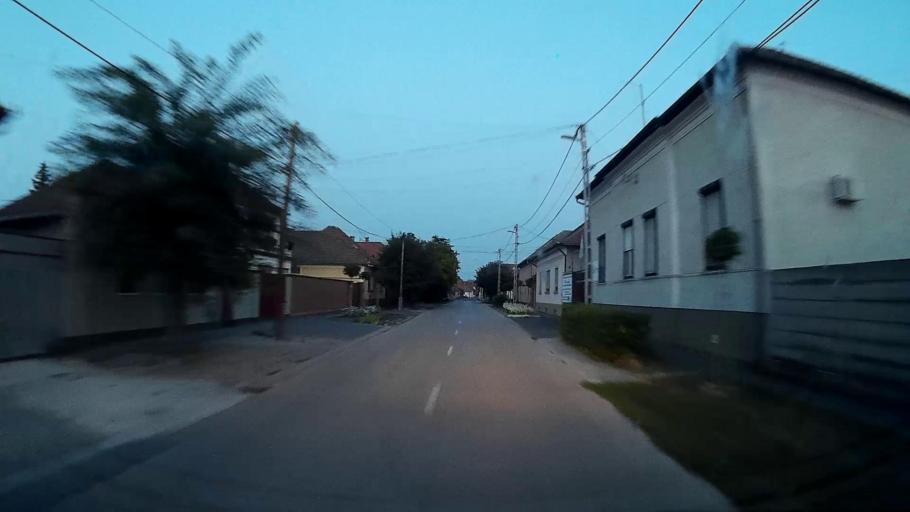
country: HU
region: Pest
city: Cegled
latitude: 47.1715
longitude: 19.7894
